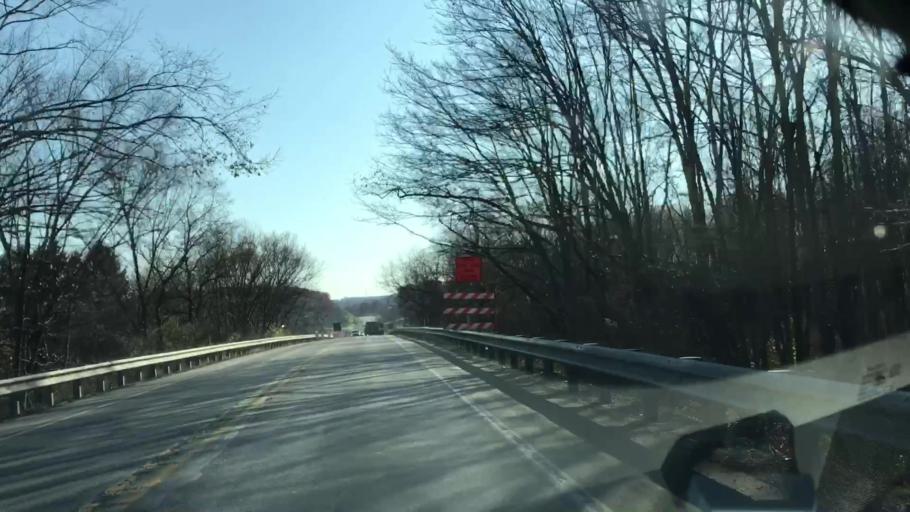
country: US
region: Pennsylvania
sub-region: Butler County
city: Mars
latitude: 40.6941
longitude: -80.0271
